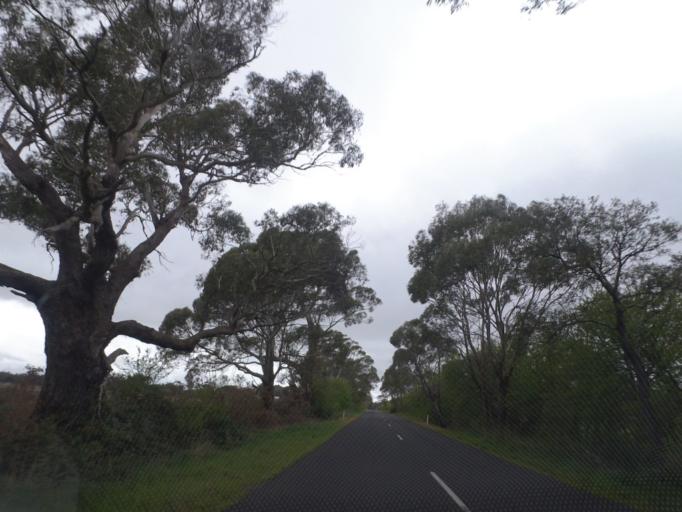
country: AU
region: Victoria
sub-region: Hume
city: Sunbury
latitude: -37.3250
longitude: 144.5722
